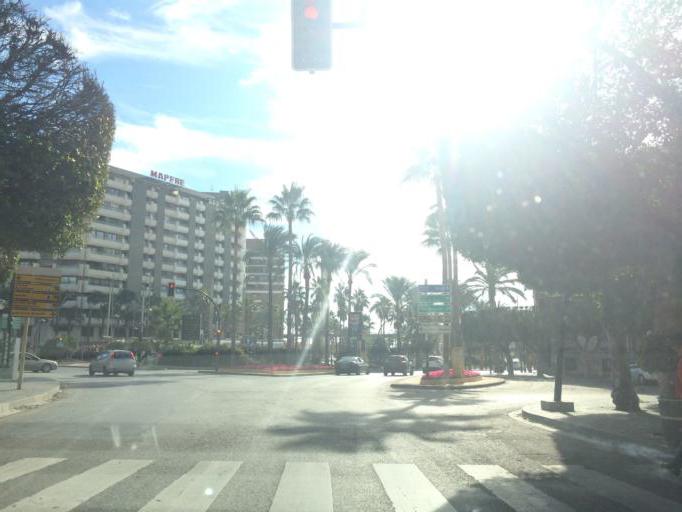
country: ES
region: Andalusia
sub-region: Provincia de Almeria
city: Almeria
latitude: 36.8357
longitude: -2.4630
